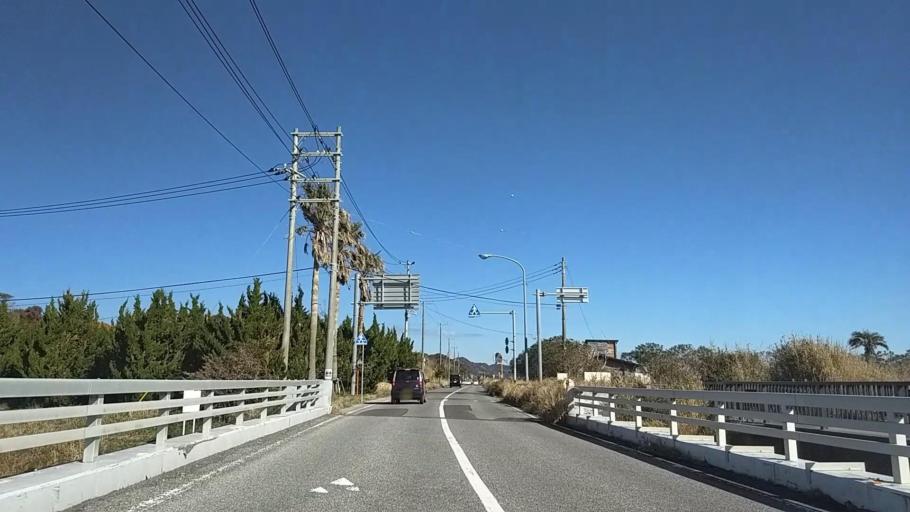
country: JP
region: Chiba
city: Tateyama
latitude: 35.0108
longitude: 139.9781
